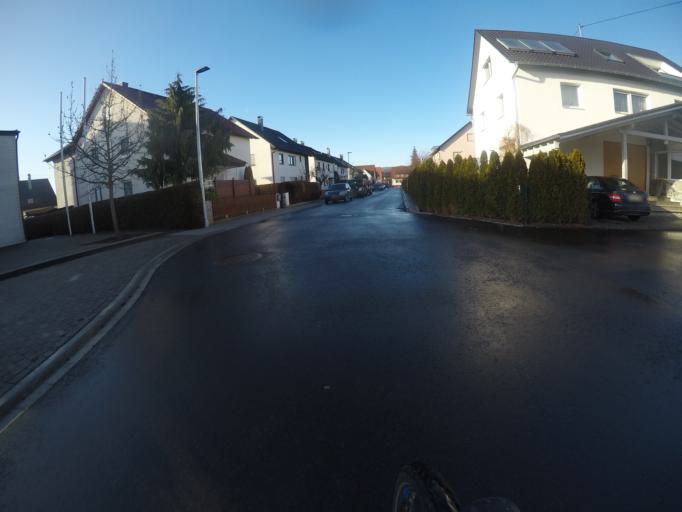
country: DE
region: Baden-Wuerttemberg
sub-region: Regierungsbezirk Stuttgart
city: Neckartailfingen
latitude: 48.6117
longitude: 9.2731
